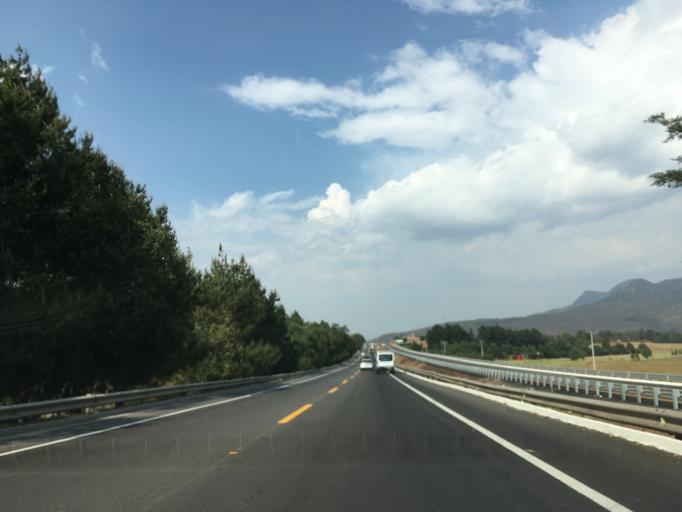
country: MX
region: Michoacan
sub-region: Patzcuaro
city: Colonia Vista Bella (Lomas del Peaje)
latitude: 19.4996
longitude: -101.5874
